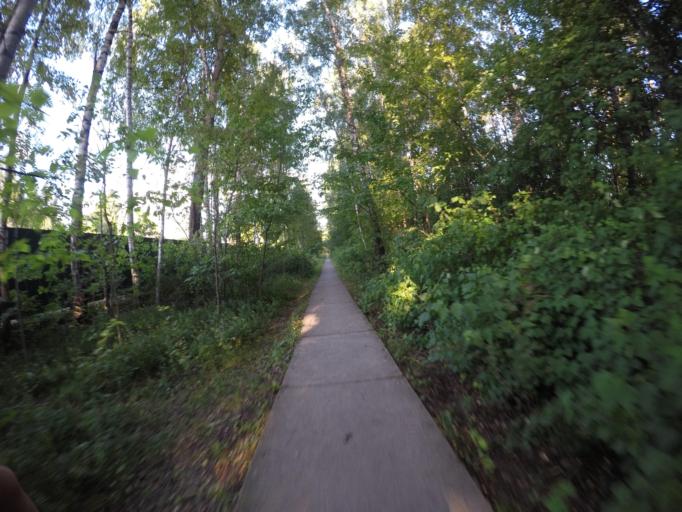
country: RU
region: Moskovskaya
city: Rechitsy
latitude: 55.6047
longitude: 38.4991
